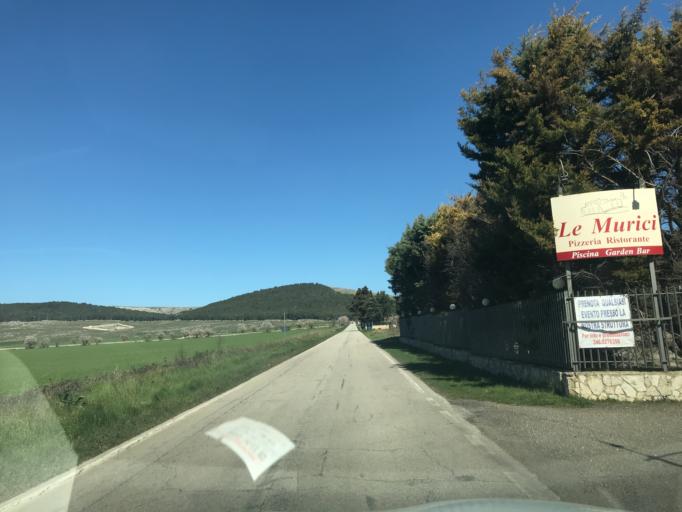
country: IT
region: Apulia
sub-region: Provincia di Bari
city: Gravina in Puglia
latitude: 40.8634
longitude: 16.4383
